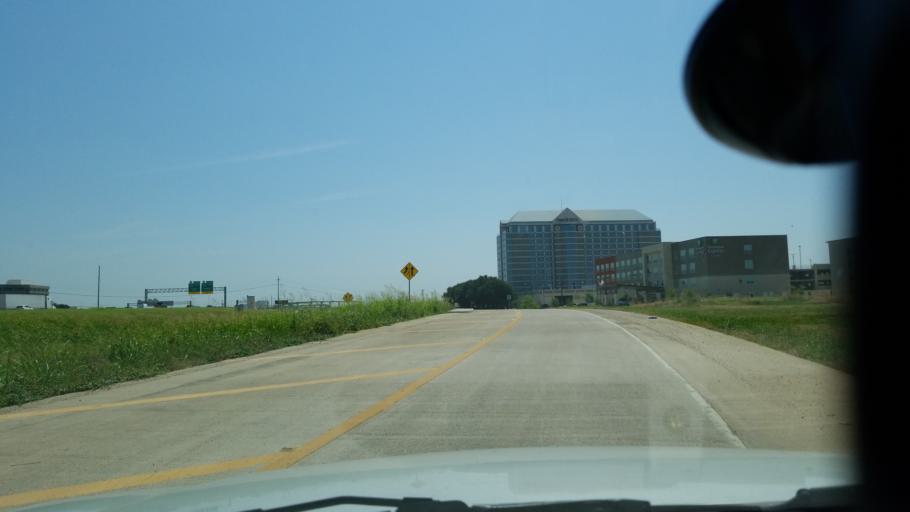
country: US
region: Texas
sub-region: Dallas County
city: Farmers Branch
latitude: 32.9067
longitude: -96.9246
